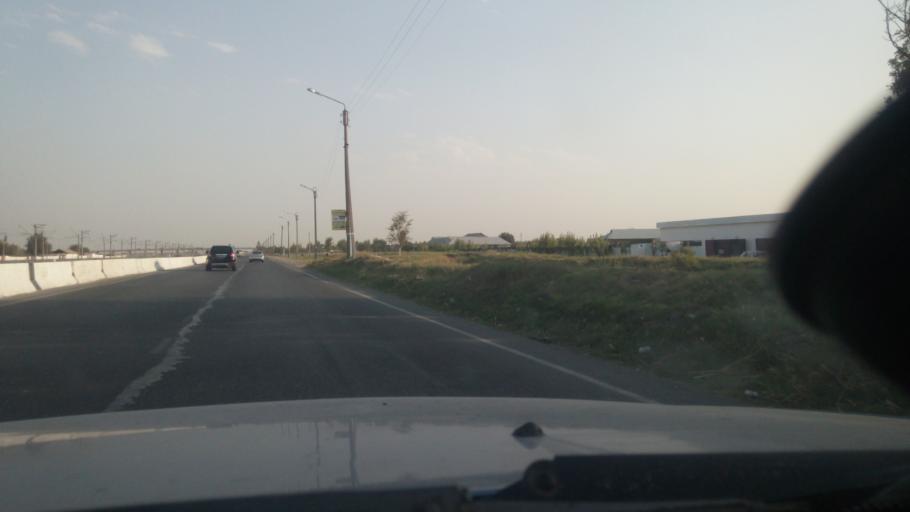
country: UZ
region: Sirdaryo
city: Guliston
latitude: 40.4832
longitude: 68.7679
